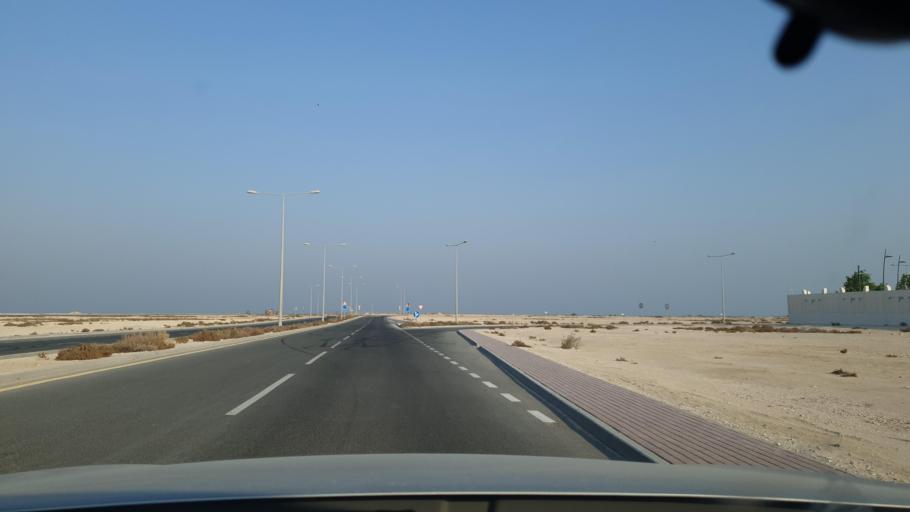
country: QA
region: Al Wakrah
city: Al Wakrah
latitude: 25.1946
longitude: 51.6134
